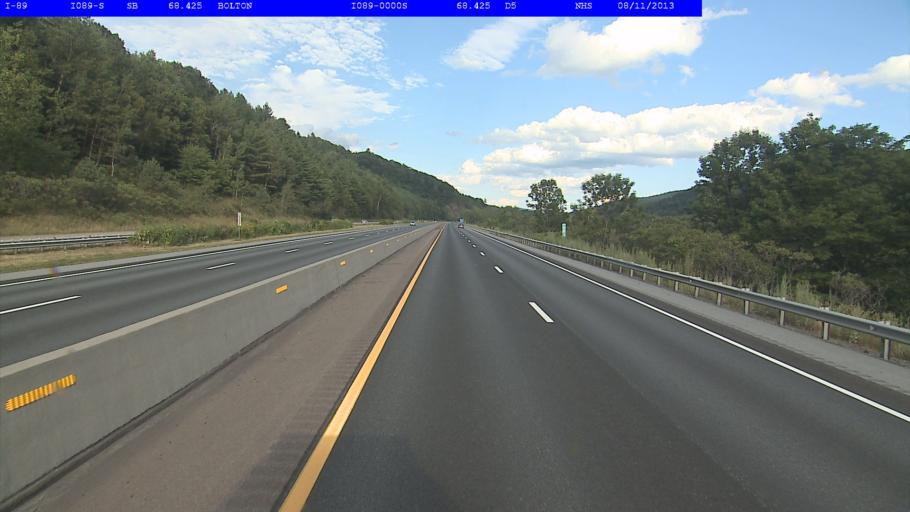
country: US
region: Vermont
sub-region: Washington County
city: Waterbury
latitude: 44.3622
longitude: -72.8381
